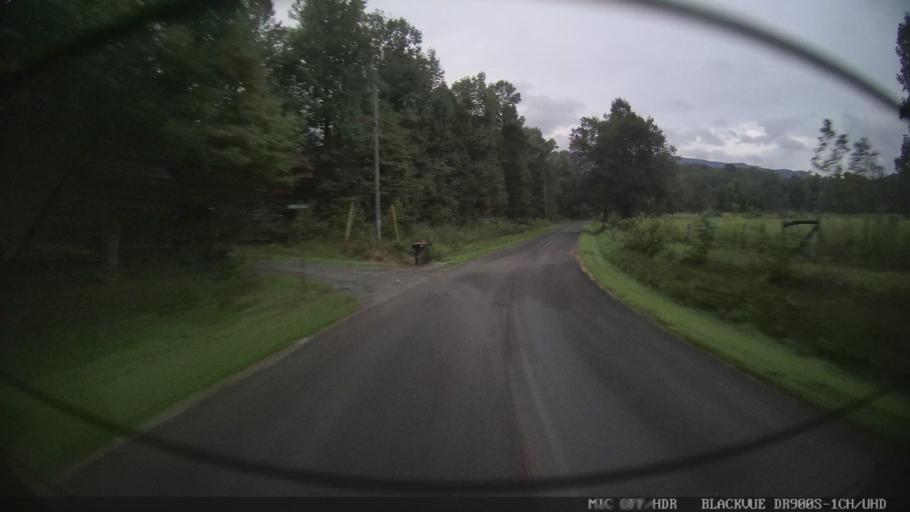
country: US
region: Georgia
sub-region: Gilmer County
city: Ellijay
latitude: 34.6814
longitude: -84.3333
